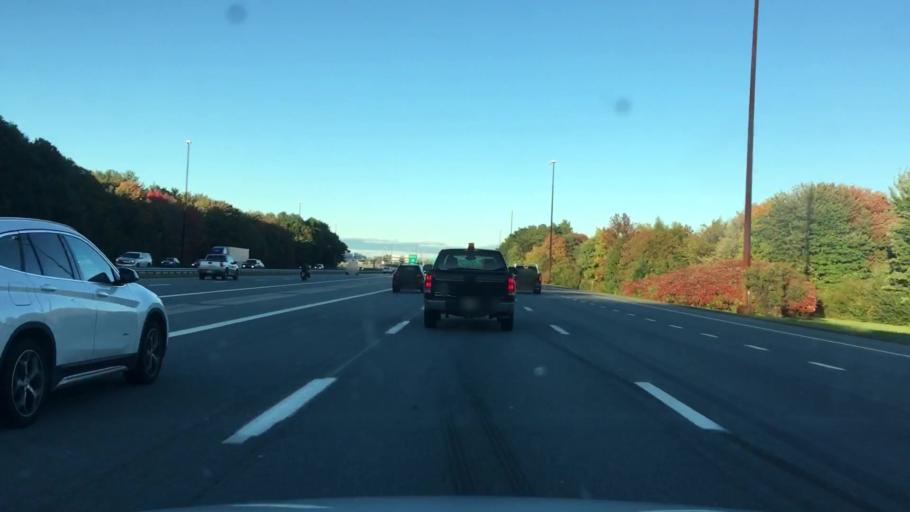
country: US
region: New Hampshire
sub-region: Rockingham County
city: Portsmouth
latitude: 43.0623
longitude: -70.7973
